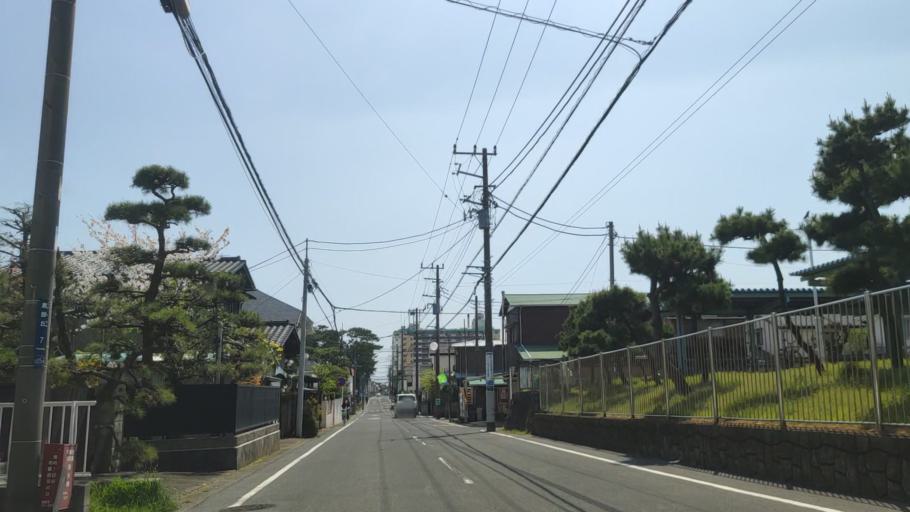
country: JP
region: Kanagawa
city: Hiratsuka
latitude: 35.3216
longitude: 139.3386
